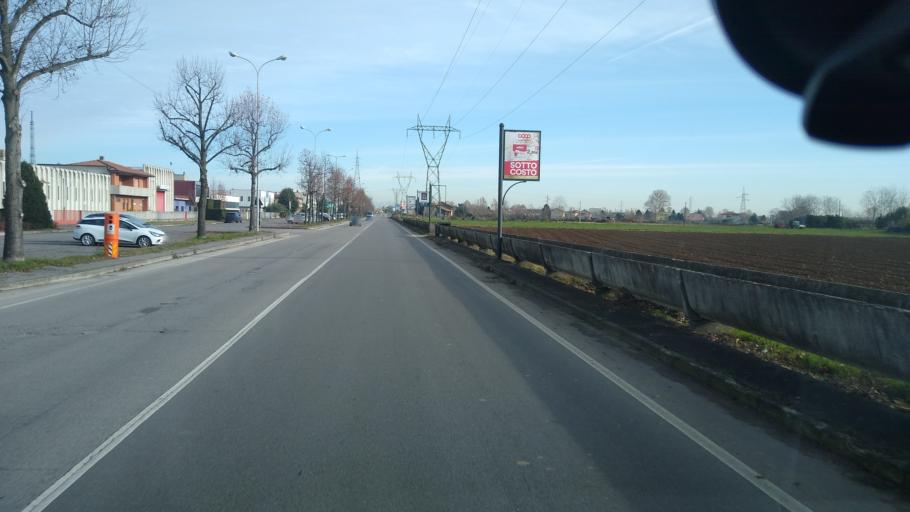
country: IT
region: Lombardy
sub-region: Provincia di Bergamo
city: Casirate d'Adda
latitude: 45.5093
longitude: 9.5735
